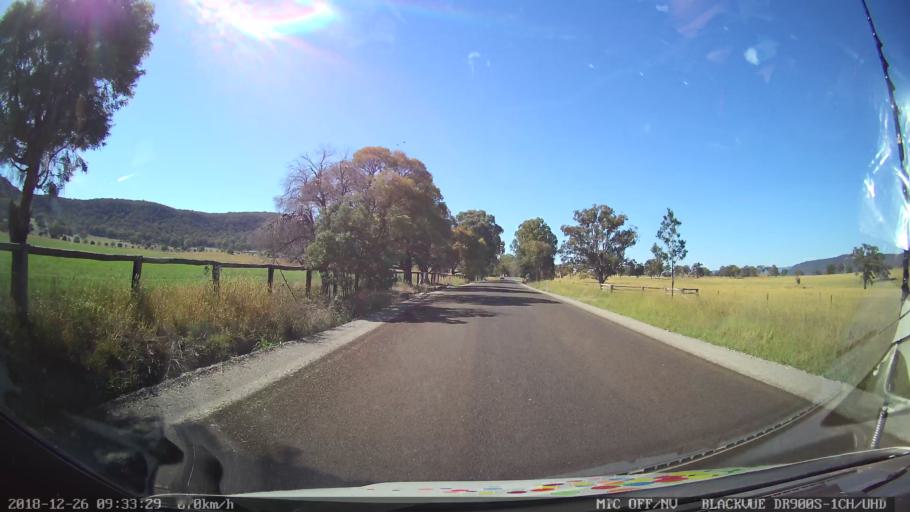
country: AU
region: New South Wales
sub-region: Mid-Western Regional
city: Kandos
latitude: -32.8952
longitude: 150.0351
